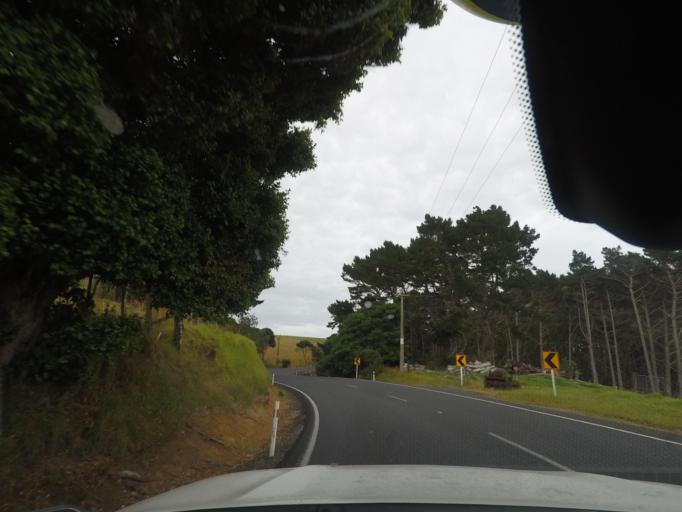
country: NZ
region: Auckland
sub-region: Auckland
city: Parakai
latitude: -36.5181
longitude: 174.2549
